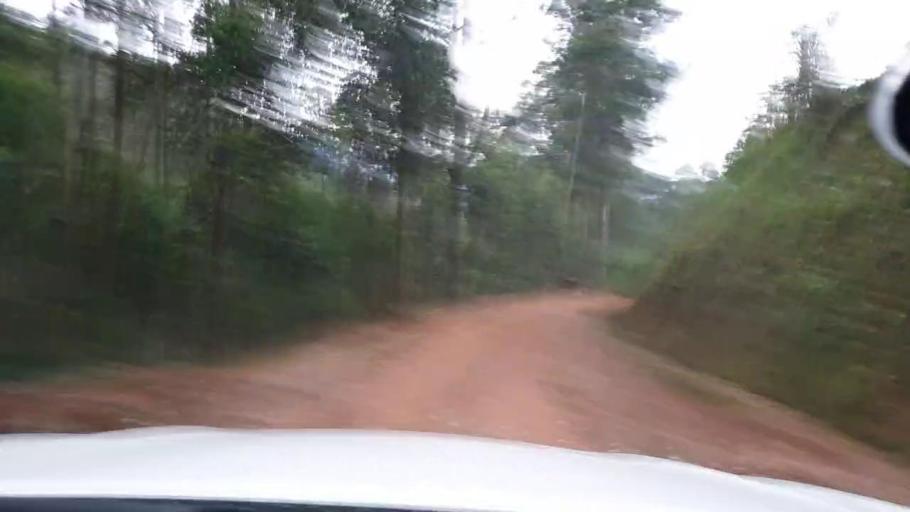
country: RW
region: Western Province
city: Cyangugu
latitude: -2.4085
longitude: 29.2046
